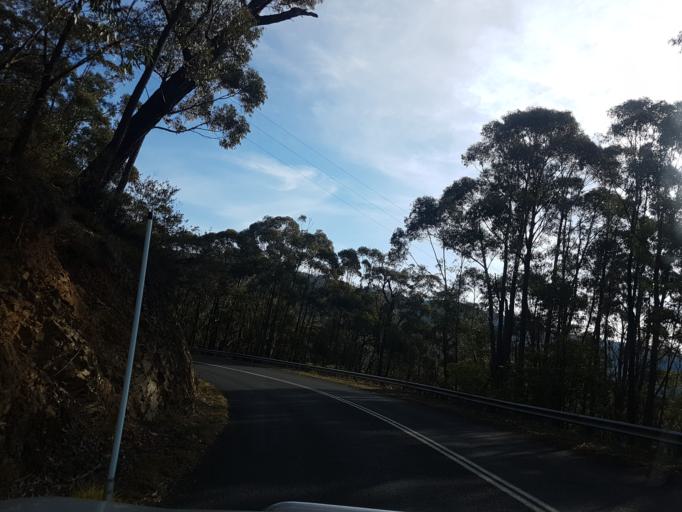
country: AU
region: Victoria
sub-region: Latrobe
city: Moe
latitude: -37.8539
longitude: 146.3960
